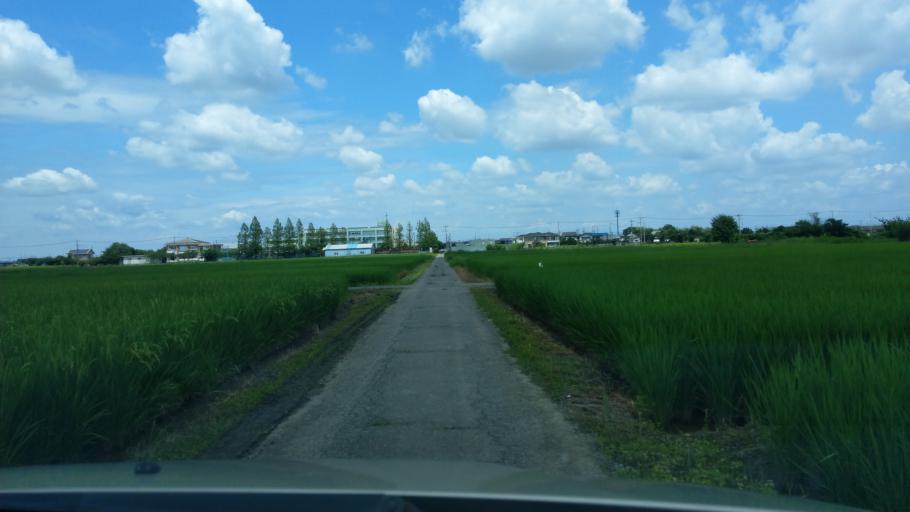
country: JP
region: Saitama
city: Yono
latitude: 35.8832
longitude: 139.5846
